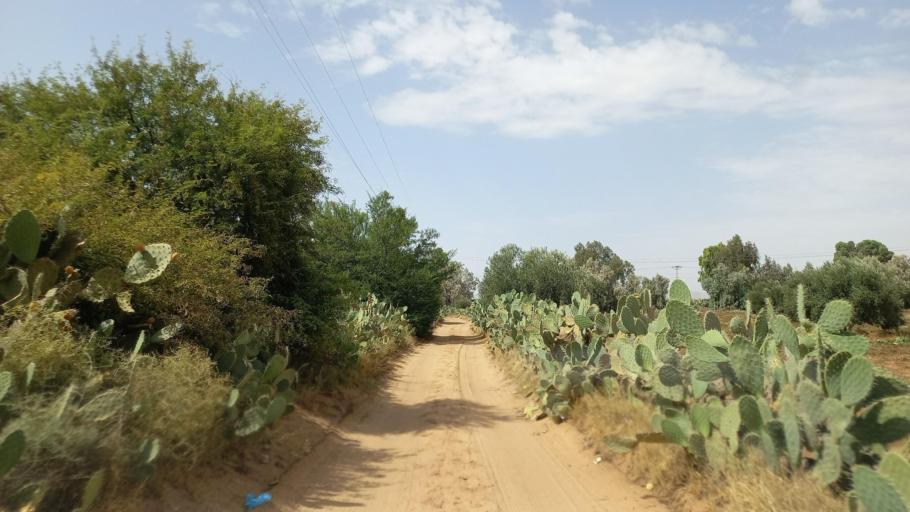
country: TN
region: Al Qasrayn
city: Kasserine
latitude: 35.2621
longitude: 9.0514
